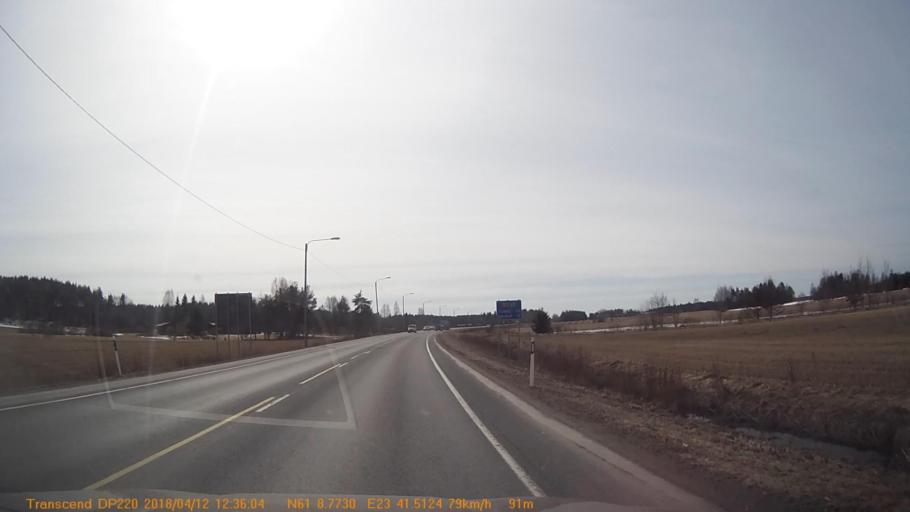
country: FI
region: Pirkanmaa
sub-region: Etelae-Pirkanmaa
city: Kylmaekoski
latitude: 61.1464
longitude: 23.6920
